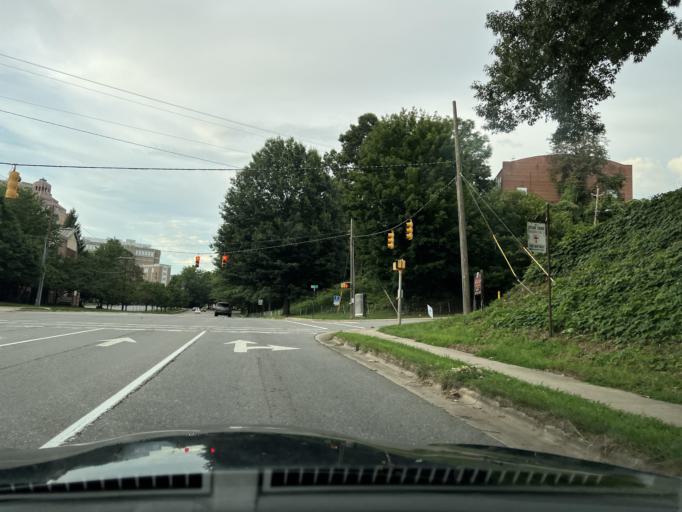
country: US
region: North Carolina
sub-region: Buncombe County
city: Asheville
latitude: 35.5921
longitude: -82.5487
